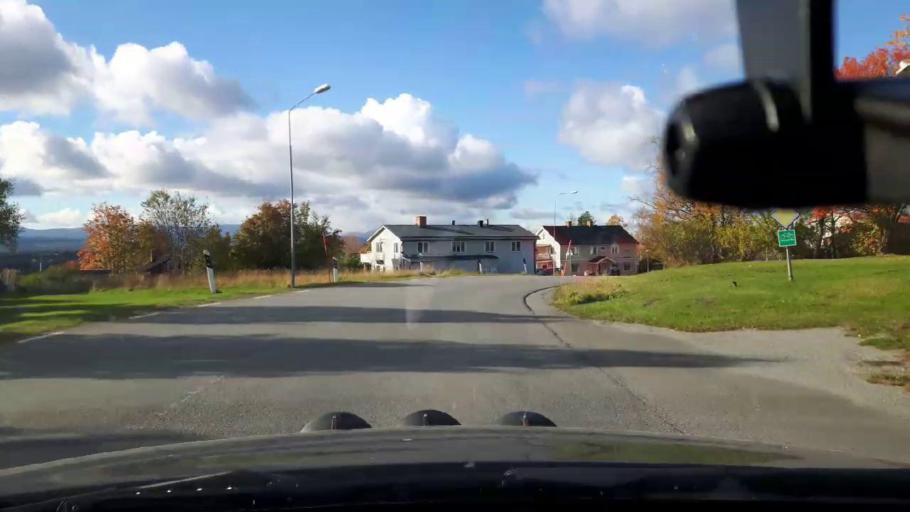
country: SE
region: Jaemtland
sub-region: Bergs Kommun
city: Hoverberg
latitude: 62.9966
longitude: 14.3935
